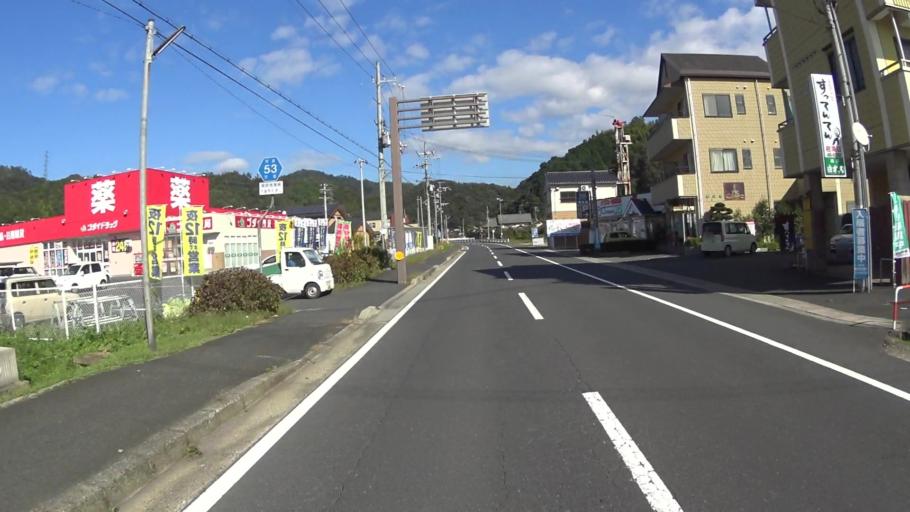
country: JP
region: Kyoto
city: Miyazu
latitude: 35.5721
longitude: 135.1613
